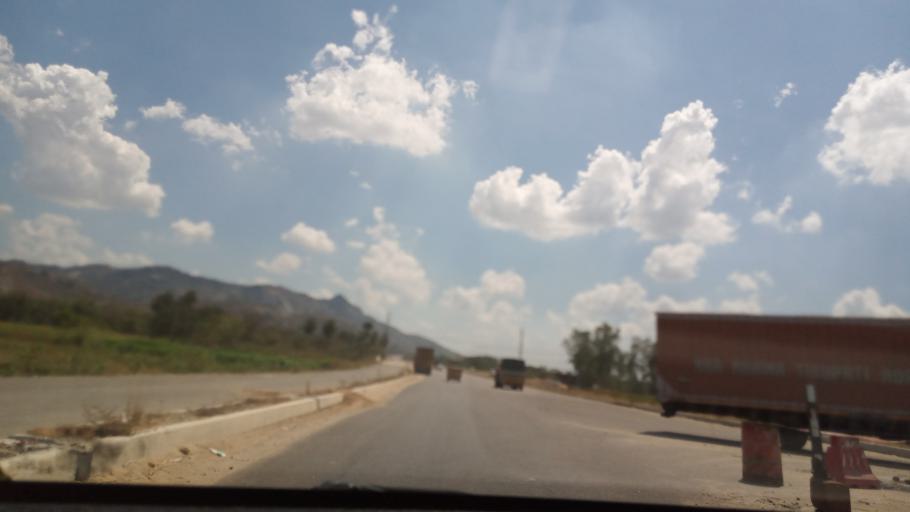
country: IN
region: Andhra Pradesh
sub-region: Chittoor
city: Pakala
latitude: 13.3506
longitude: 79.0842
